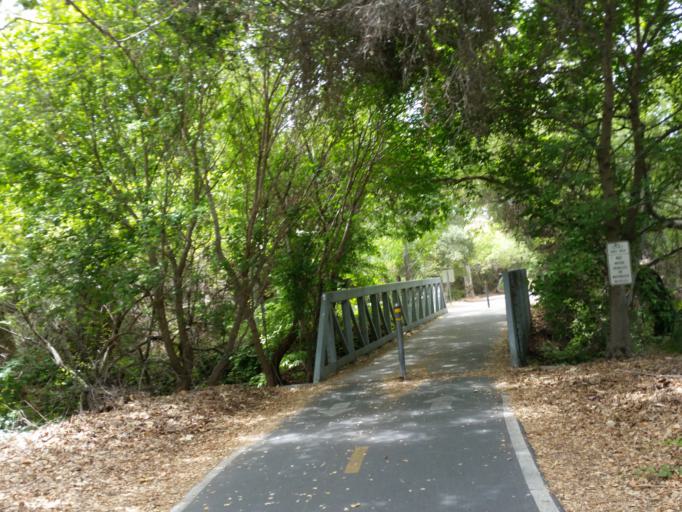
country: US
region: California
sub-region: San Luis Obispo County
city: Avila Beach
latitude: 35.1885
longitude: -120.7144
